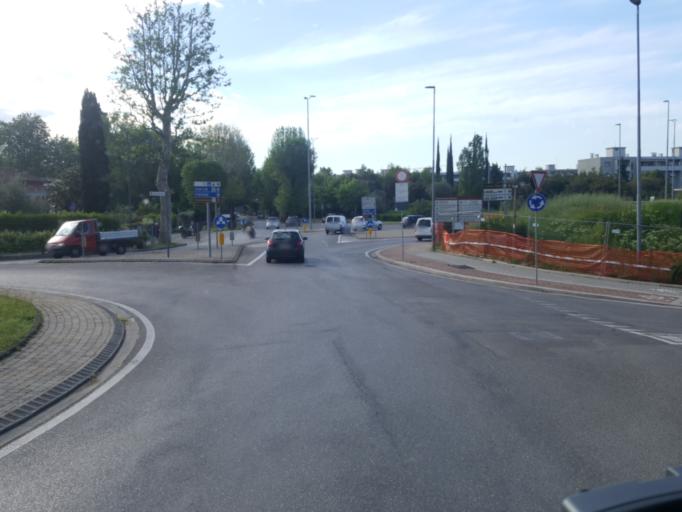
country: IT
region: Tuscany
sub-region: Province of Florence
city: Calenzano
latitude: 43.8448
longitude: 11.1800
